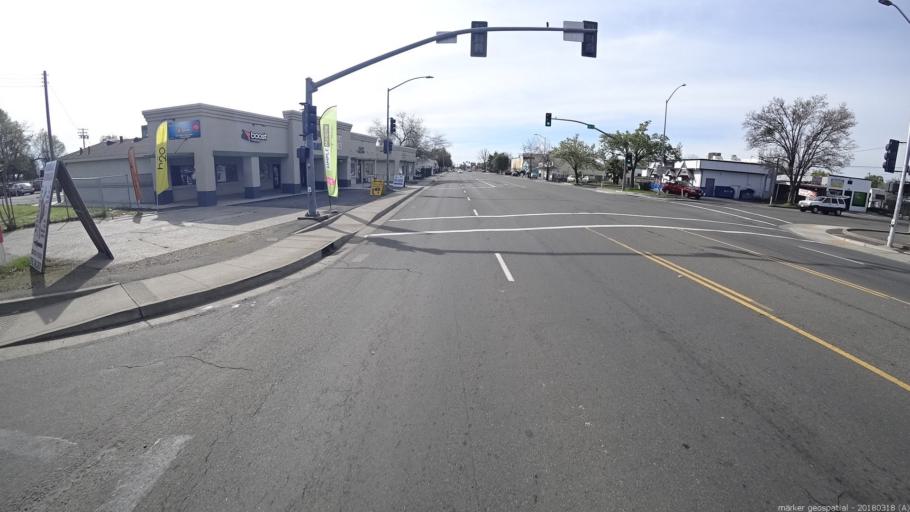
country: US
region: California
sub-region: Sacramento County
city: Parkway
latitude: 38.5290
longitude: -121.4727
